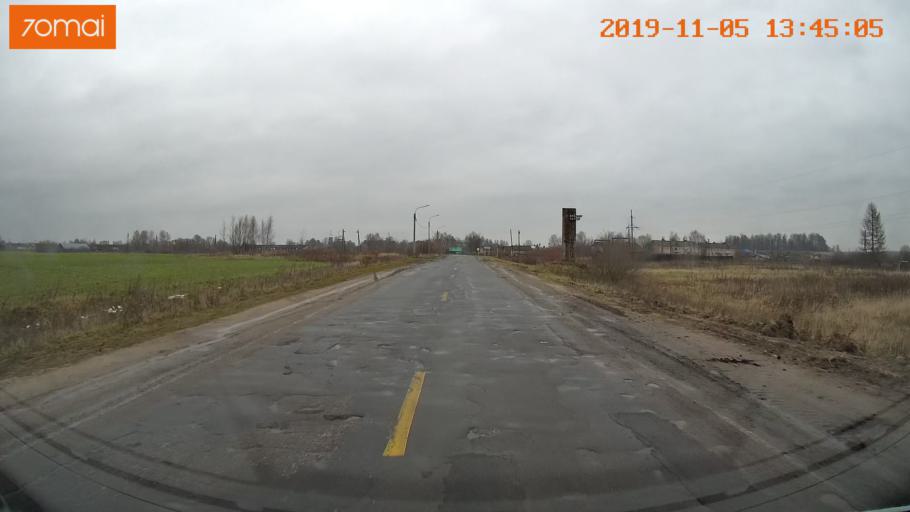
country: RU
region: Ivanovo
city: Shuya
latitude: 56.9859
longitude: 41.4121
